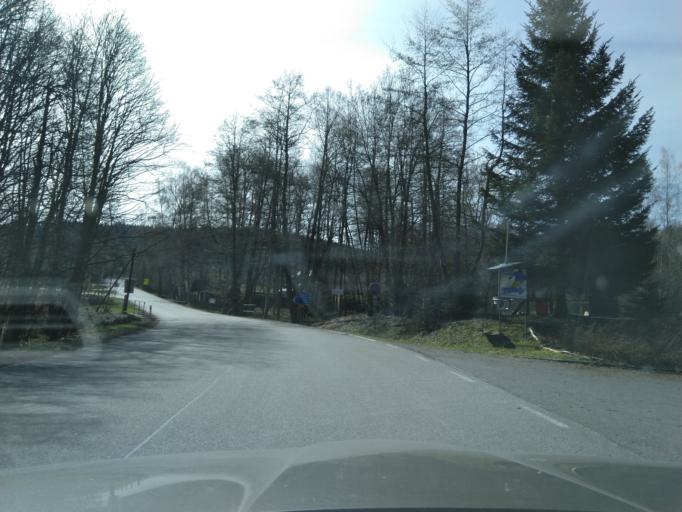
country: CZ
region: Jihocesky
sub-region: Okres Prachatice
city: Stachy
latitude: 49.0732
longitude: 13.6335
